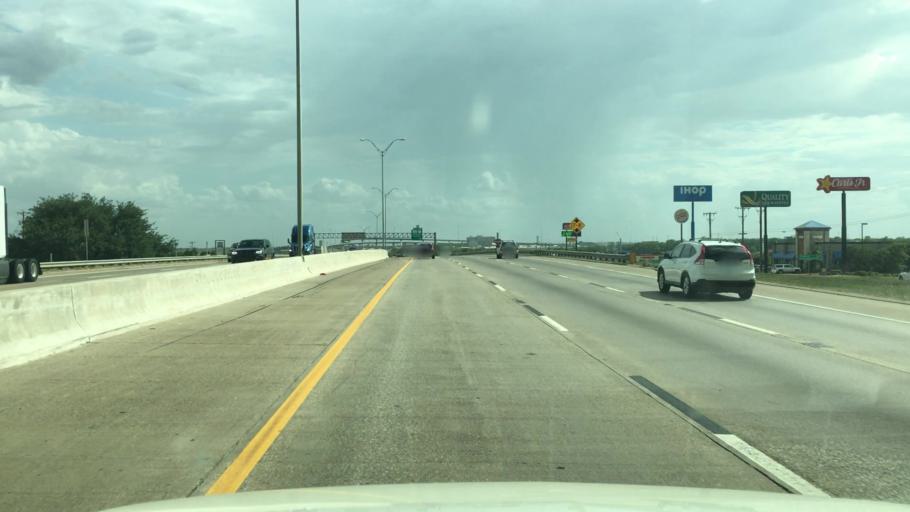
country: US
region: Texas
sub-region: McLennan County
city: Beverly
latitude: 31.5102
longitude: -97.1419
